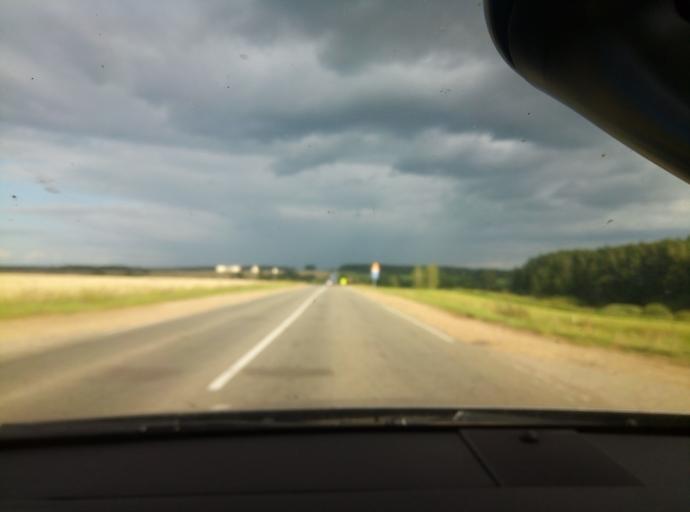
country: RU
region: Kaluga
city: Babynino
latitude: 54.5169
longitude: 35.7417
